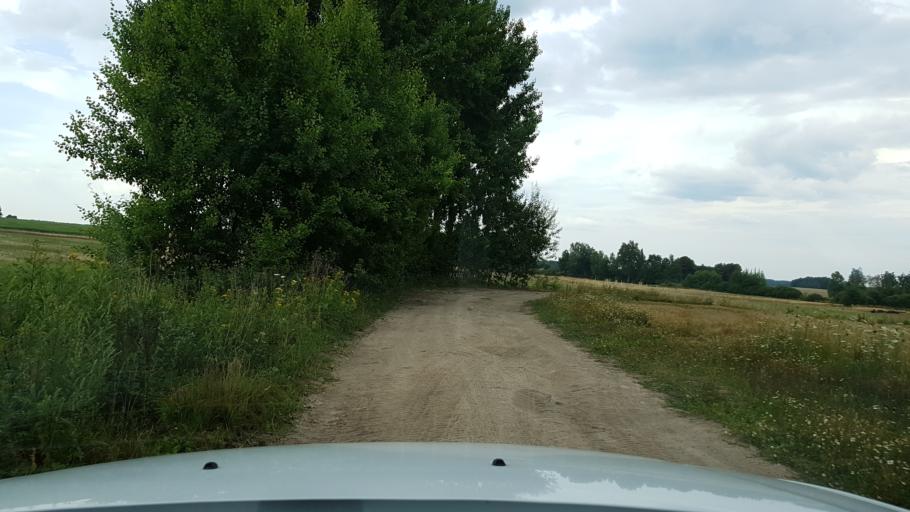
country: PL
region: West Pomeranian Voivodeship
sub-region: Powiat walecki
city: Walcz
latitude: 53.3728
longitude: 16.3436
